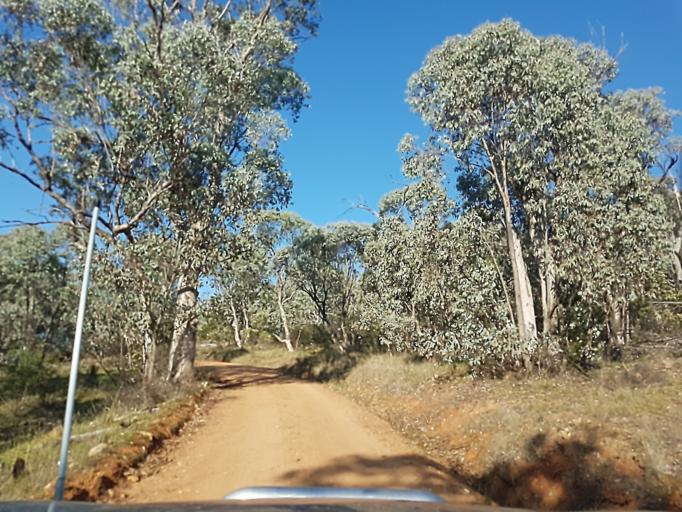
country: AU
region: New South Wales
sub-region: Snowy River
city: Jindabyne
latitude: -36.9554
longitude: 148.3628
